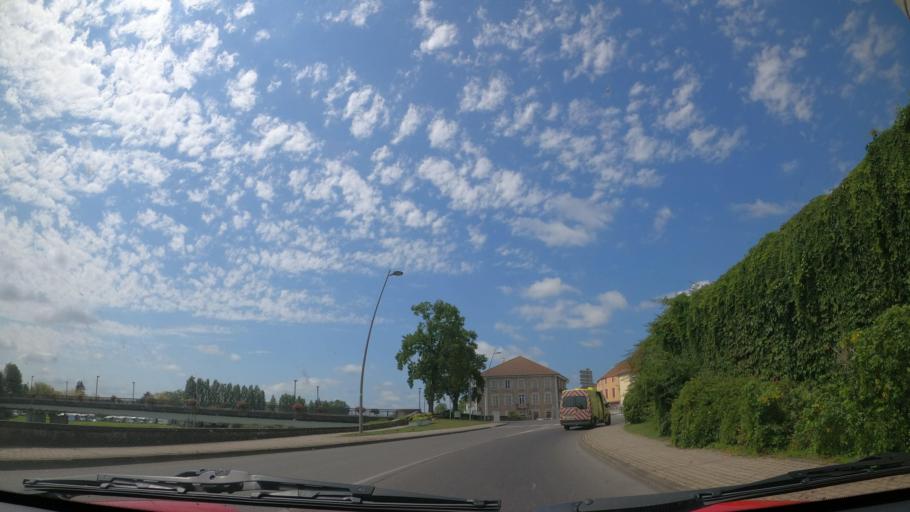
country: FR
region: Aquitaine
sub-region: Departement des Landes
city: Peyrehorade
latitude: 43.5437
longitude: -1.1043
